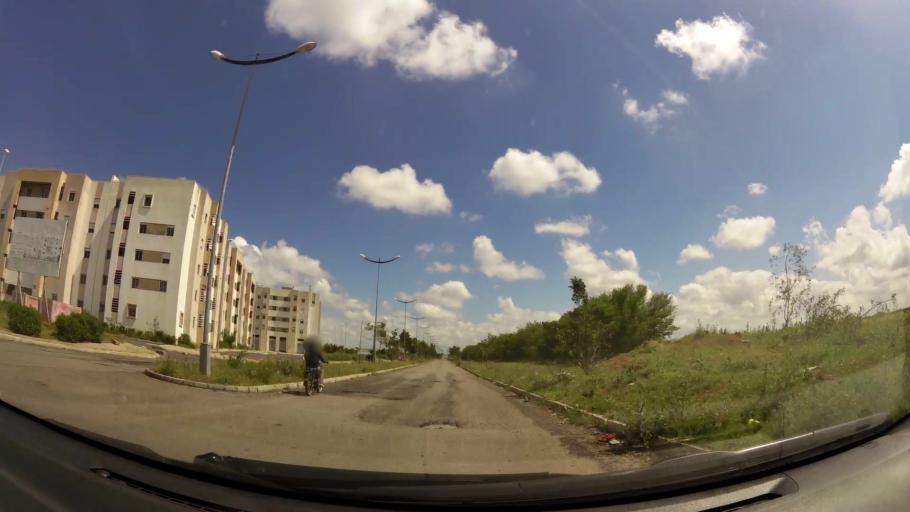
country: MA
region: Grand Casablanca
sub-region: Nouaceur
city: Dar Bouazza
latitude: 33.4172
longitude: -7.8337
